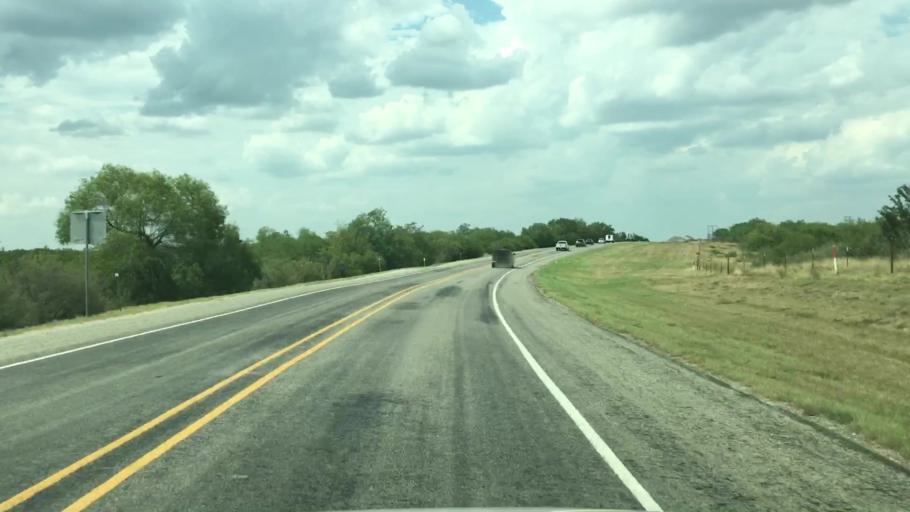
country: US
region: Texas
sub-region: Live Oak County
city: Three Rivers
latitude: 28.6430
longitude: -98.2840
